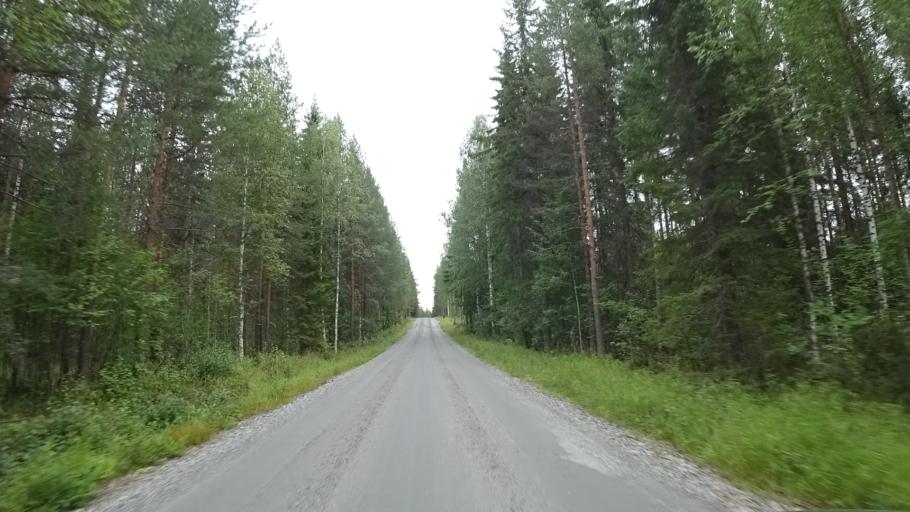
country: FI
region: North Karelia
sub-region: Pielisen Karjala
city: Lieksa
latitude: 63.3754
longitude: 30.3608
